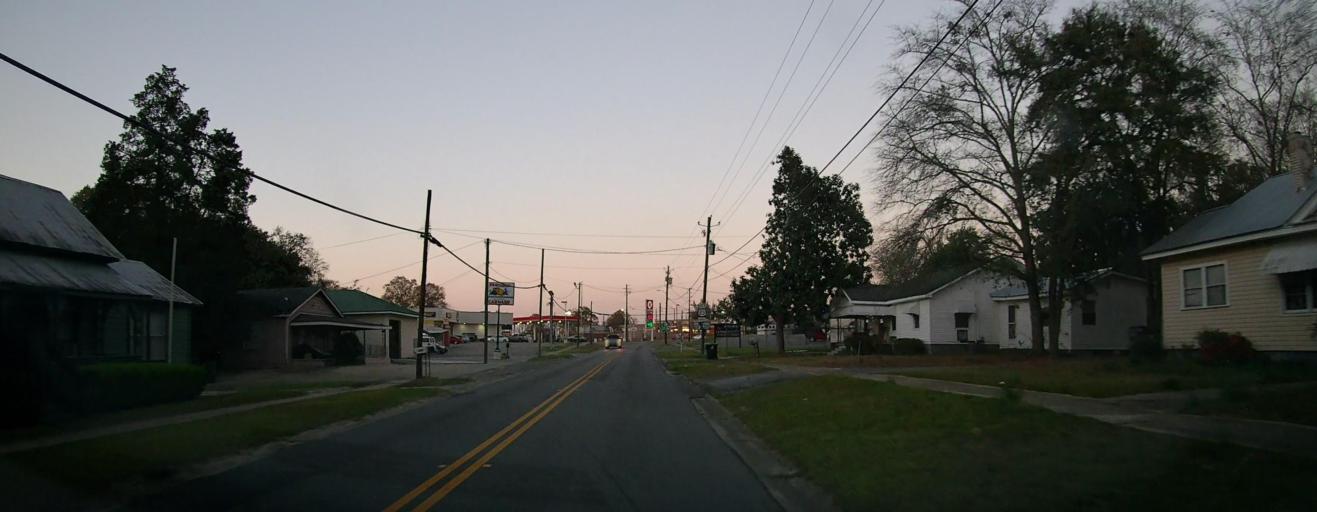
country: US
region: Georgia
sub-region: Dodge County
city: Eastman
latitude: 32.1914
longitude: -83.1762
